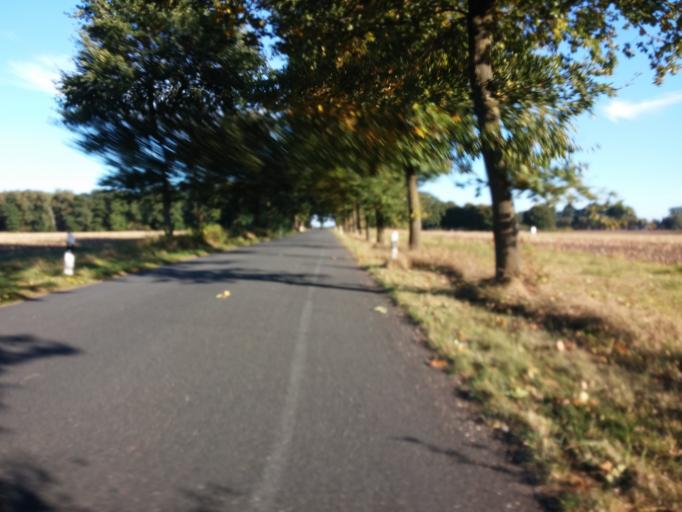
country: DE
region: North Rhine-Westphalia
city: Dorsten
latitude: 51.6478
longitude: 6.9890
